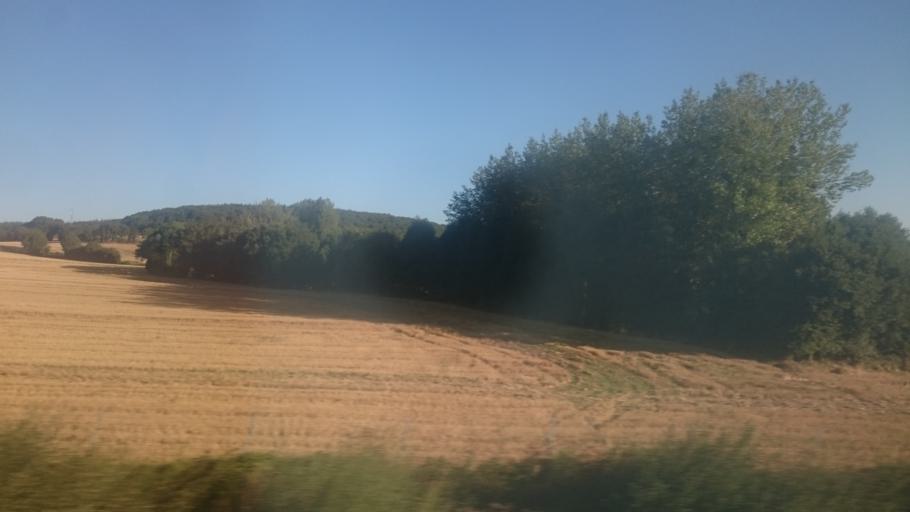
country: FR
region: Pays de la Loire
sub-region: Departement de la Sarthe
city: Vibraye
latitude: 48.0841
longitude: 0.8308
